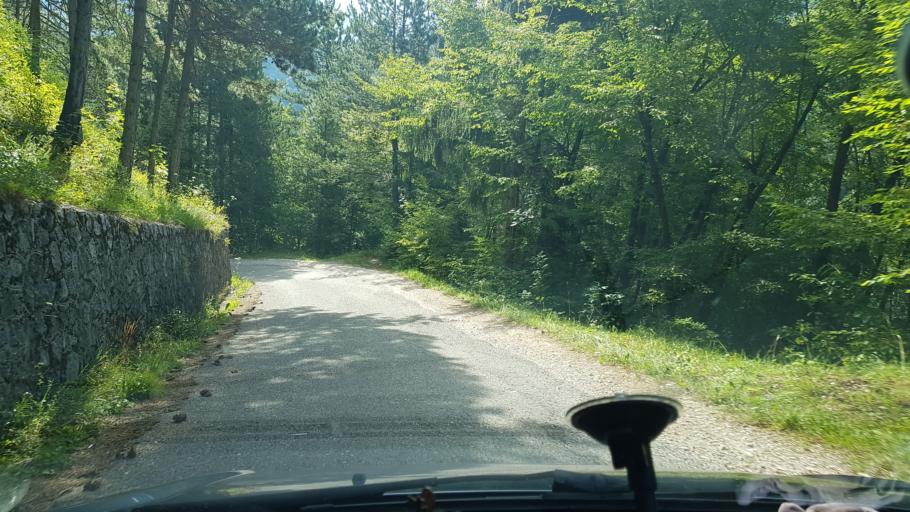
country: IT
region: Friuli Venezia Giulia
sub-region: Provincia di Udine
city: Prato
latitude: 46.3589
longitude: 13.3571
